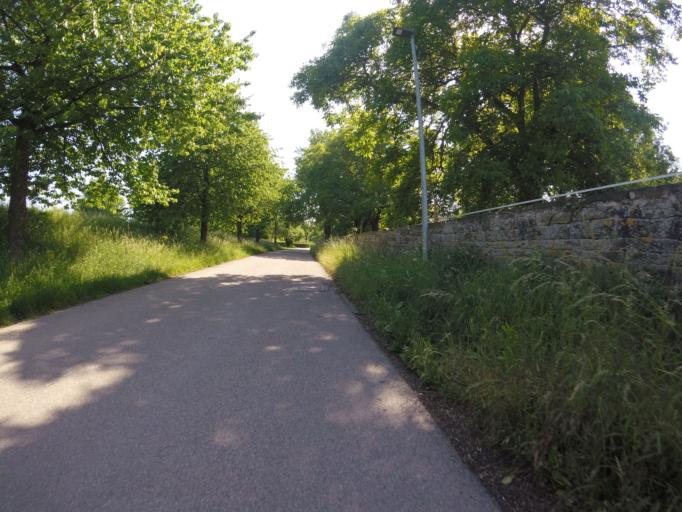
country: DE
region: Baden-Wuerttemberg
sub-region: Regierungsbezirk Stuttgart
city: Steinheim am der Murr
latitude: 48.9753
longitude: 9.2919
